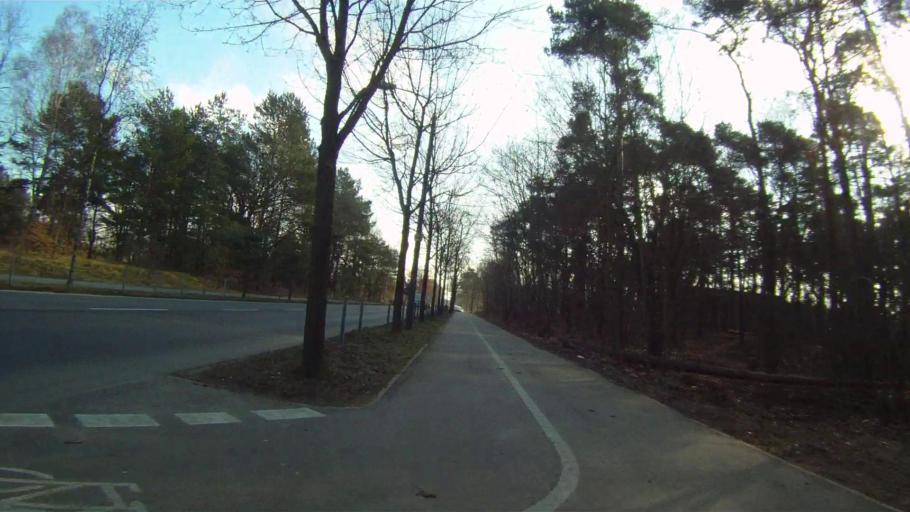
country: DE
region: Berlin
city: Rahnsdorf
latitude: 52.4354
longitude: 13.7009
